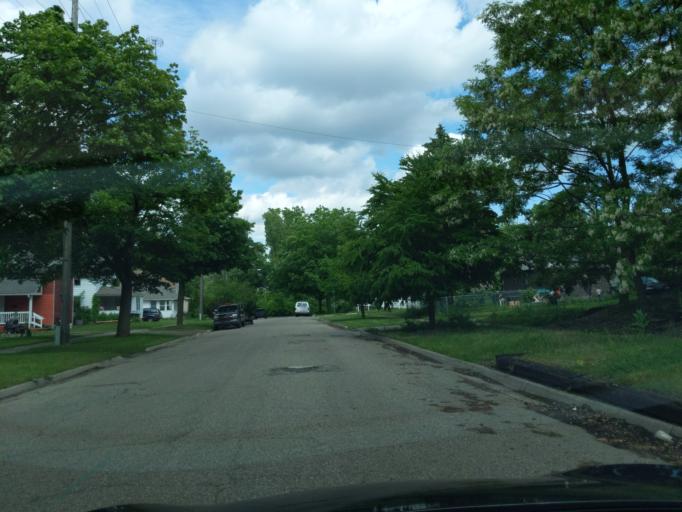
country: US
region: Michigan
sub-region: Ingham County
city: Lansing
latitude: 42.7231
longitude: -84.5506
